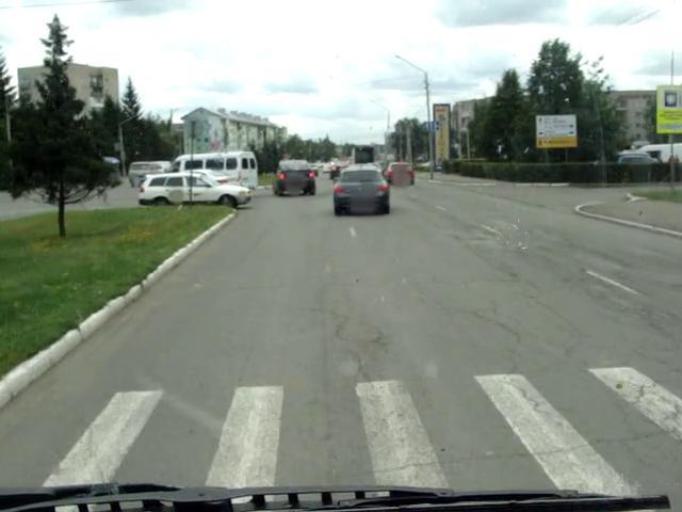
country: RU
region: Altai Krai
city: Biysk
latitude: 52.5446
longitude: 85.2161
